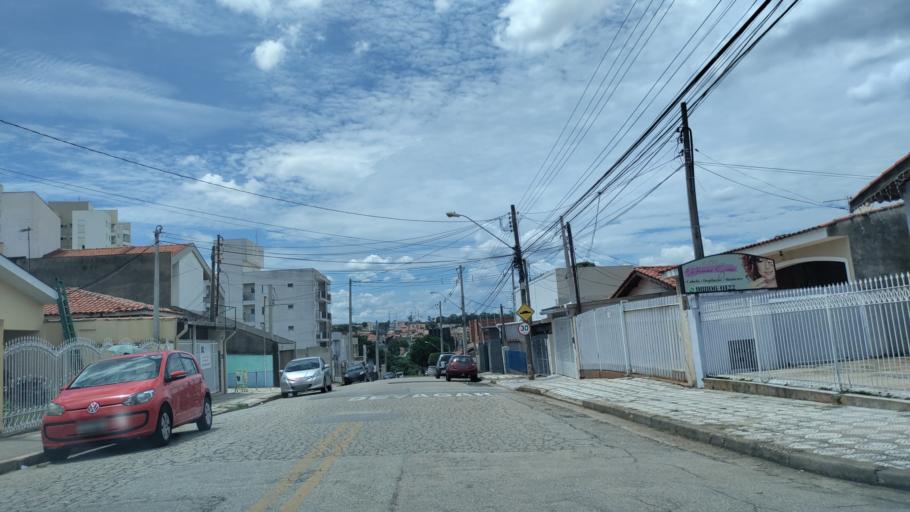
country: BR
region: Sao Paulo
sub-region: Sorocaba
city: Sorocaba
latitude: -23.4796
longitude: -47.4443
